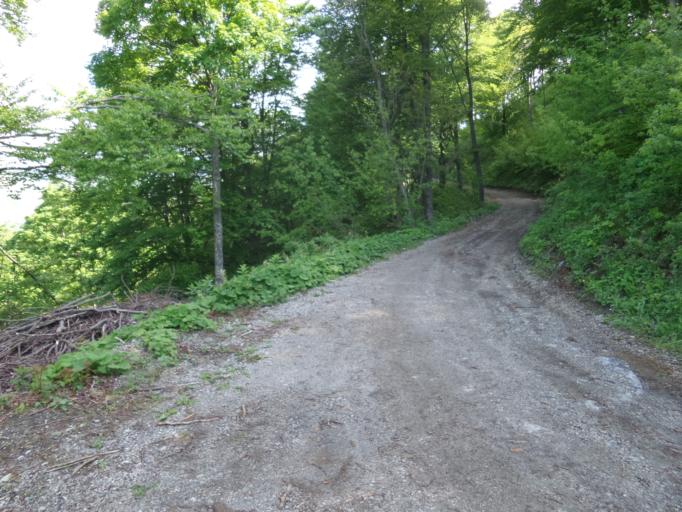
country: IT
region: Lombardy
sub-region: Provincia di Lecco
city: Moggio
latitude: 45.9243
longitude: 9.5117
